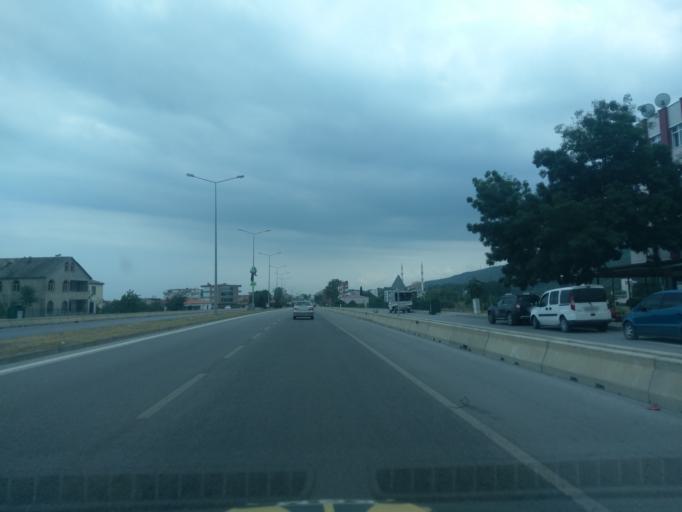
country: TR
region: Samsun
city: Taflan
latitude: 41.4063
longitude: 36.1810
